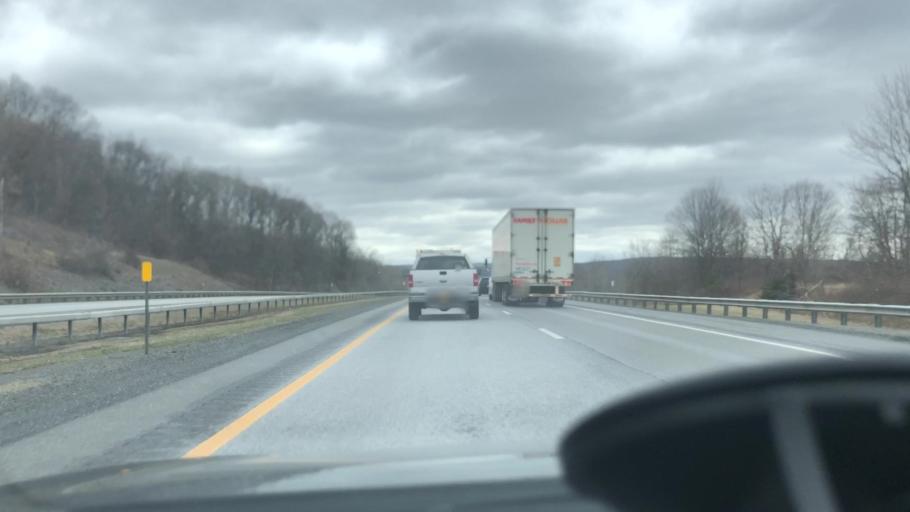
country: US
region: New York
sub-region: Herkimer County
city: Ilion
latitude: 43.0262
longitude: -75.0313
